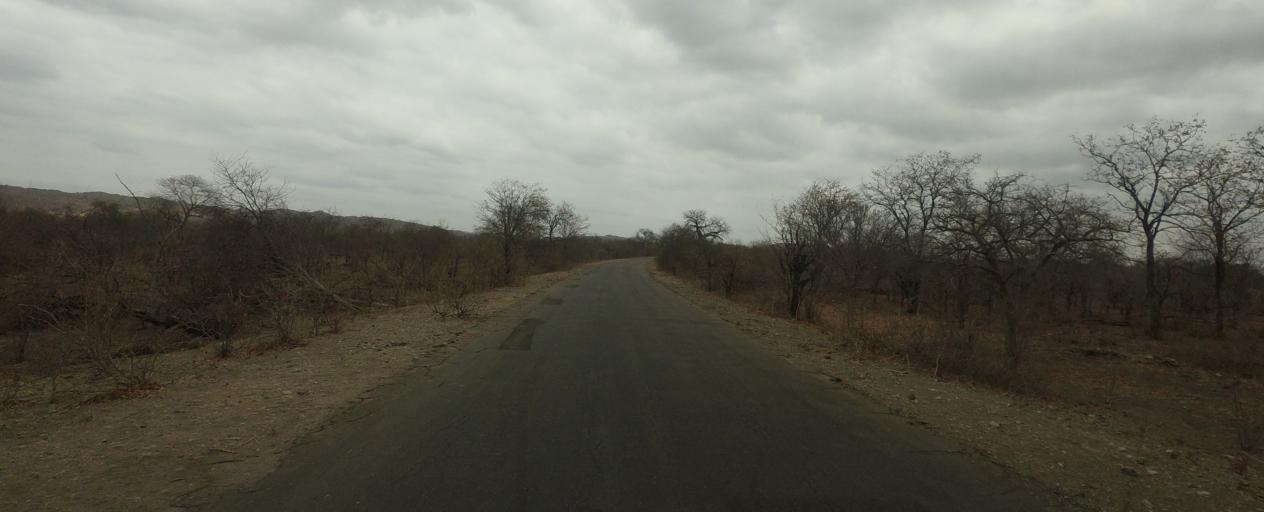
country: ZA
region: Limpopo
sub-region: Vhembe District Municipality
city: Mutale
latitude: -22.4029
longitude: 31.2013
